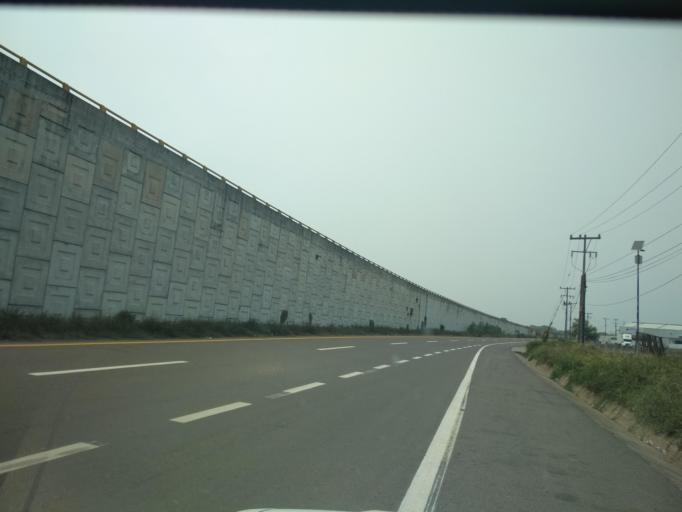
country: MX
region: Veracruz
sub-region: Veracruz
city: Delfino Victoria (Santa Fe)
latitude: 19.1896
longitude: -96.2747
